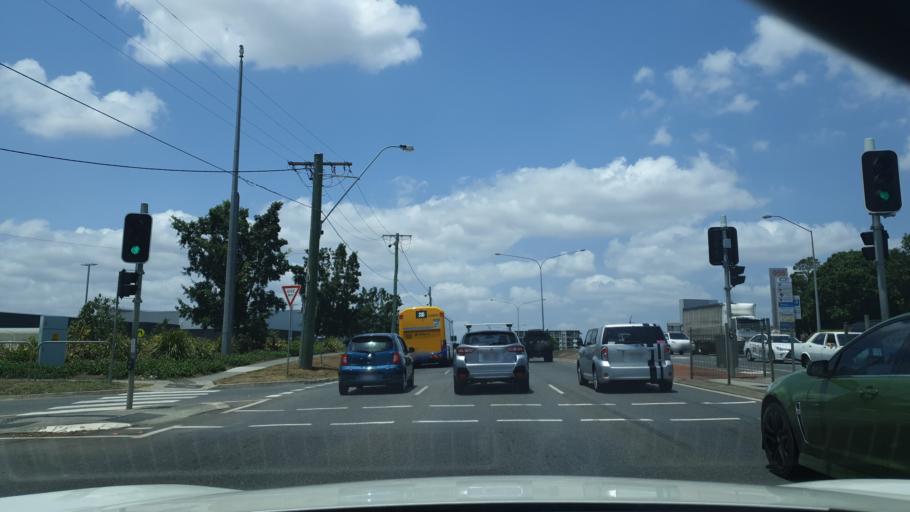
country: AU
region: Queensland
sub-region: Brisbane
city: Chermside West
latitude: -27.3817
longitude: 153.0300
